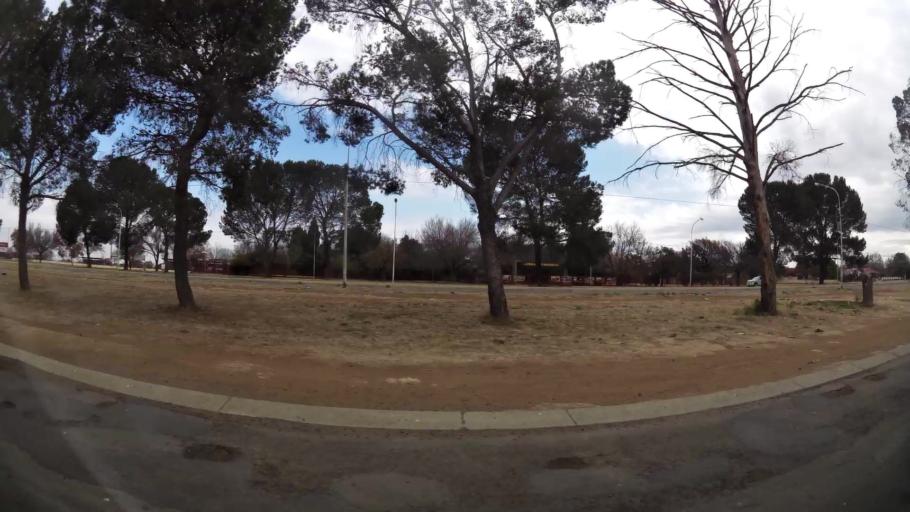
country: ZA
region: Orange Free State
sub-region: Fezile Dabi District Municipality
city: Kroonstad
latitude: -27.6371
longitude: 27.2339
